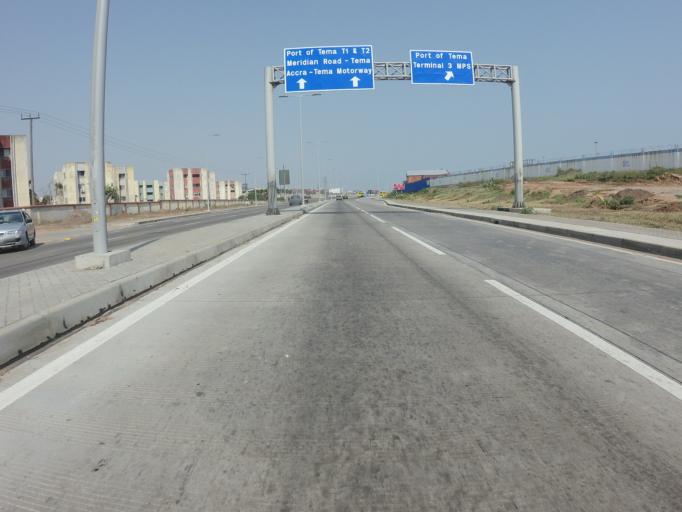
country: GH
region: Greater Accra
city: Tema
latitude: 5.6160
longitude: -0.0248
